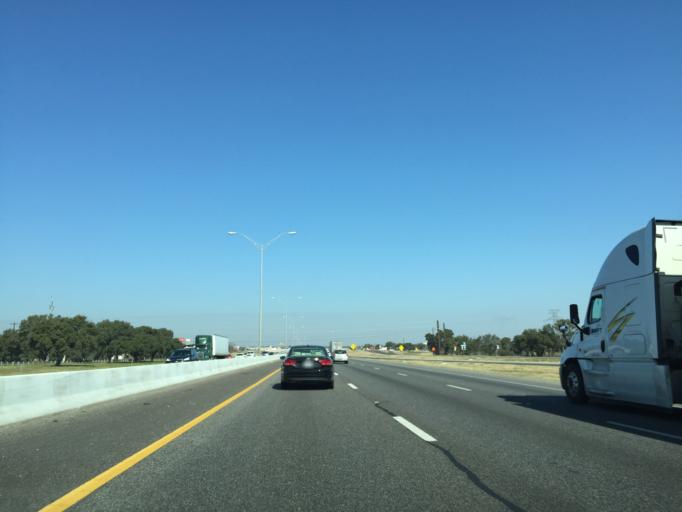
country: US
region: Texas
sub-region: Williamson County
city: Georgetown
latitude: 30.6152
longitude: -97.6880
